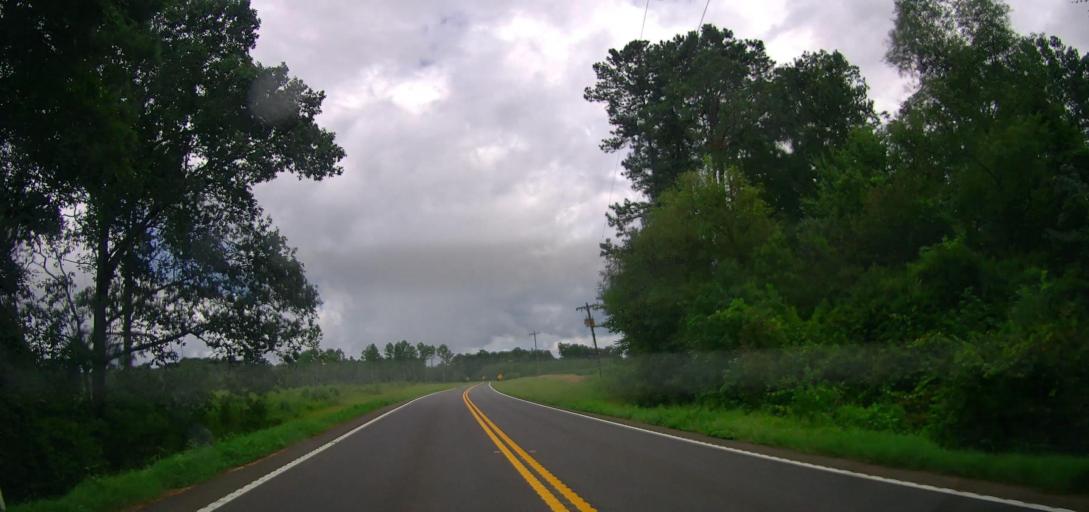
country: US
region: Georgia
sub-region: Pulaski County
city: Hawkinsville
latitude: 32.1377
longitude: -83.5570
